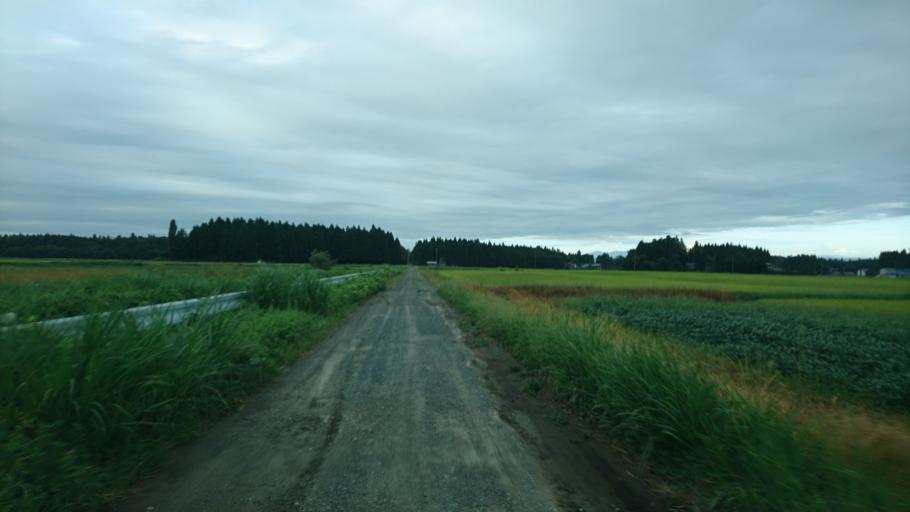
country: JP
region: Iwate
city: Kitakami
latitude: 39.3254
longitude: 141.0330
